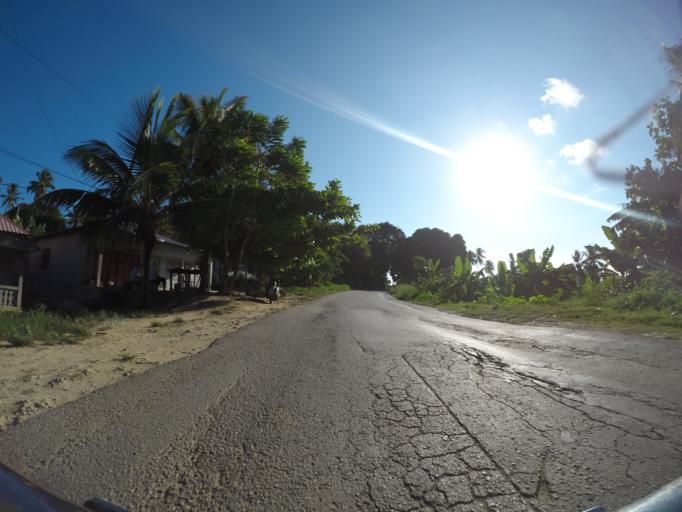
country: TZ
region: Pemba South
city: Chake Chake
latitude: -5.2852
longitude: 39.7647
